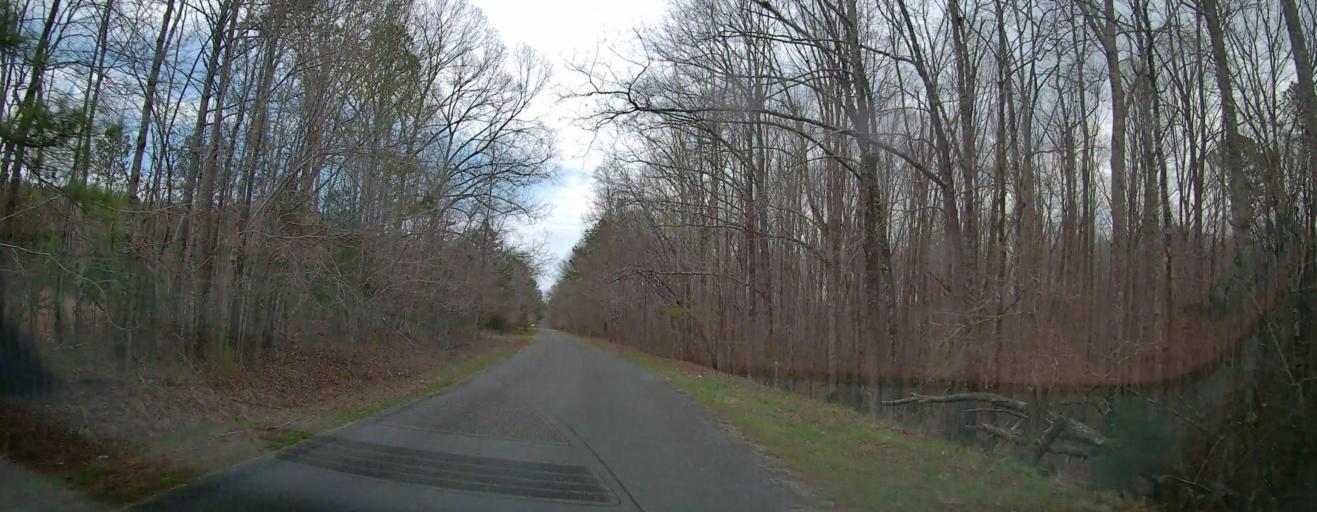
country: US
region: Alabama
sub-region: Marion County
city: Hamilton
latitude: 34.1991
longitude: -88.1843
